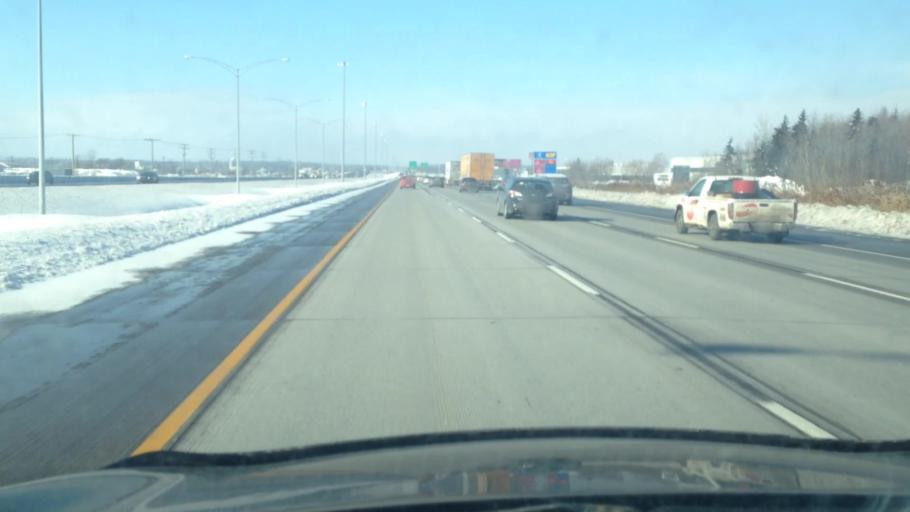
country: CA
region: Quebec
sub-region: Laurentides
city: Blainville
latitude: 45.6868
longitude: -73.9280
